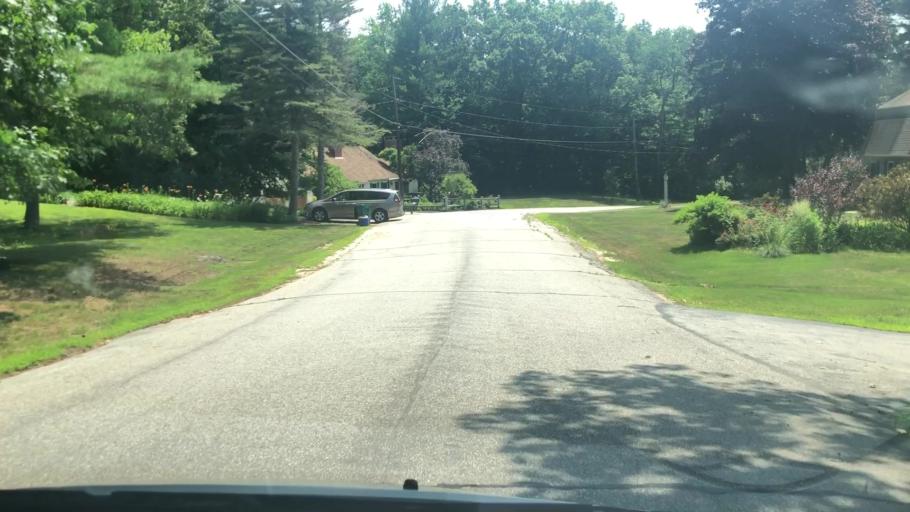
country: US
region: New Hampshire
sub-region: Hillsborough County
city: Milford
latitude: 42.8711
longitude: -71.6198
